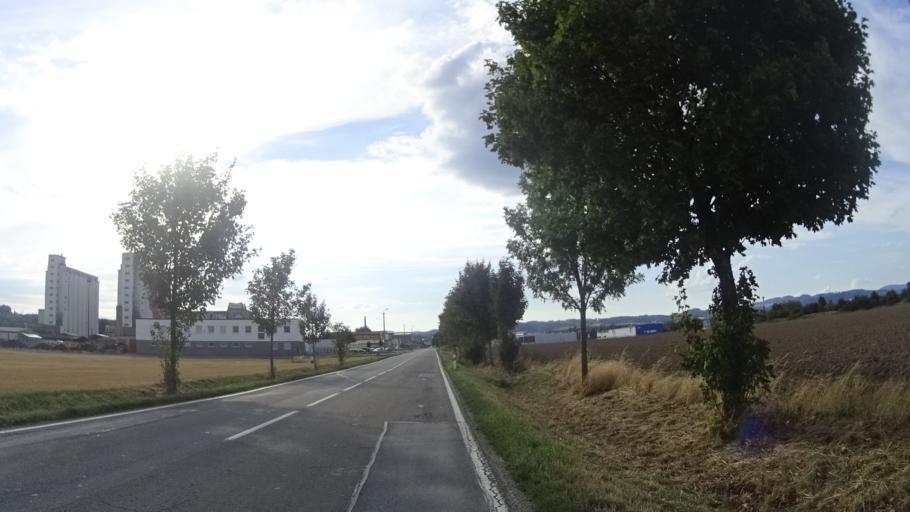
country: CZ
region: Olomoucky
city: Zabreh
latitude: 49.8751
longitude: 16.8971
